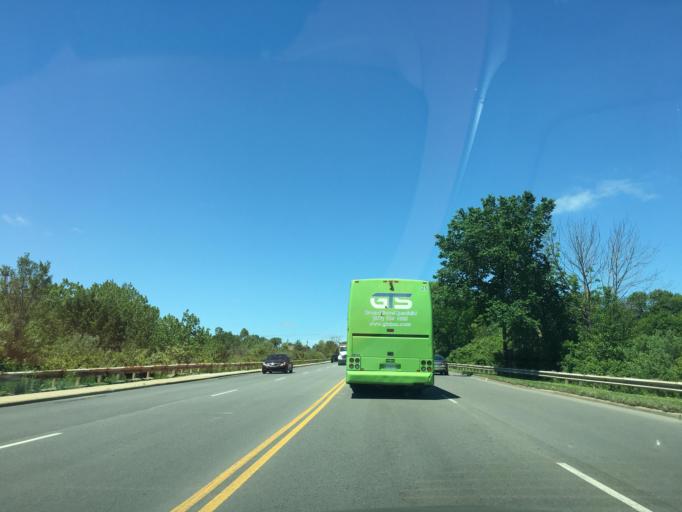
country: US
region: Ohio
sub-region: Cuyahoga County
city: Independence
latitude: 41.3942
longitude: -81.6352
